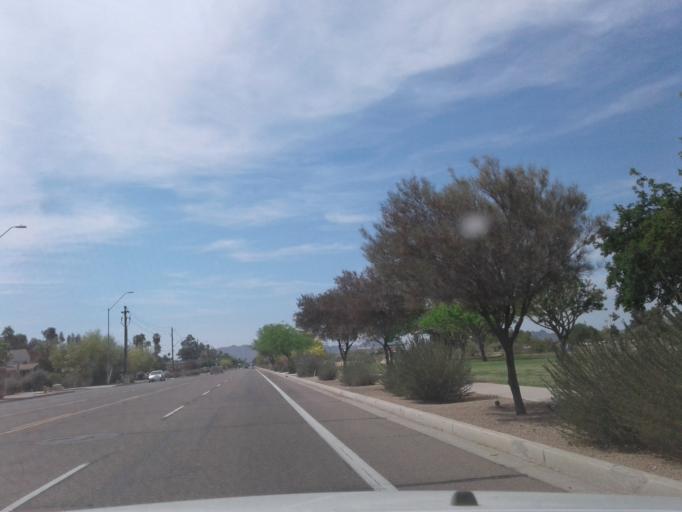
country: US
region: Arizona
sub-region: Maricopa County
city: Paradise Valley
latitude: 33.6523
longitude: -111.9963
